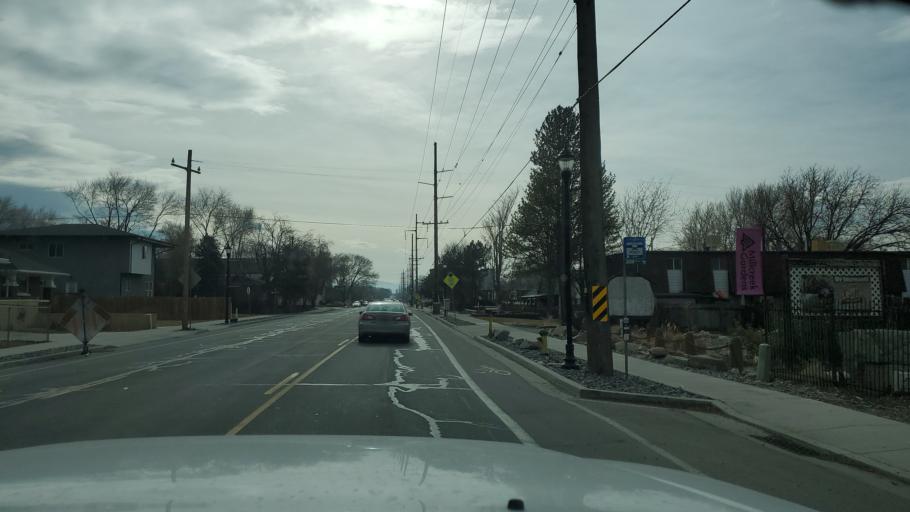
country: US
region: Utah
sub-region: Salt Lake County
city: Millcreek
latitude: 40.6946
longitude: -111.8655
